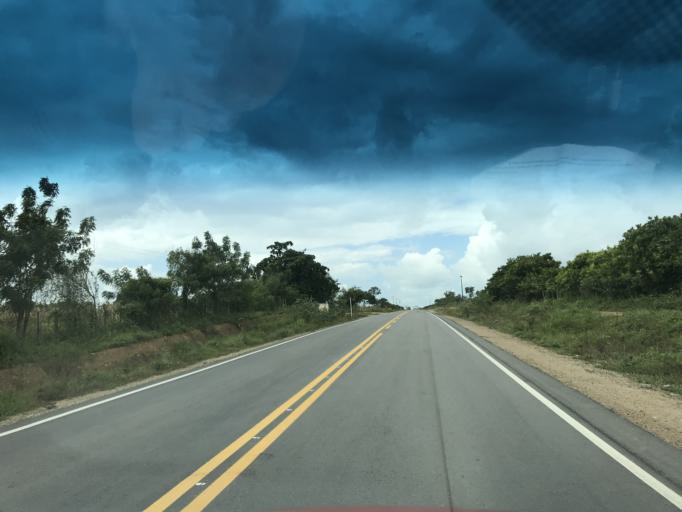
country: BR
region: Bahia
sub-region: Conceicao Do Almeida
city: Conceicao do Almeida
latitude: -12.6669
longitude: -39.2818
